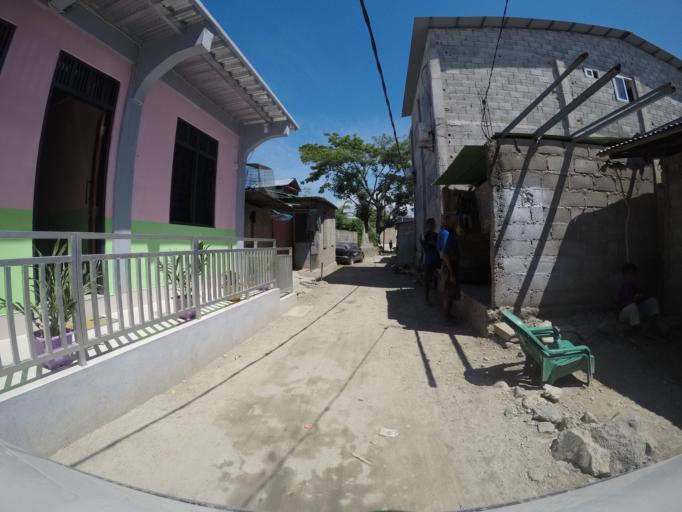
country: TL
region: Dili
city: Dili
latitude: -8.5522
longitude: 125.5372
